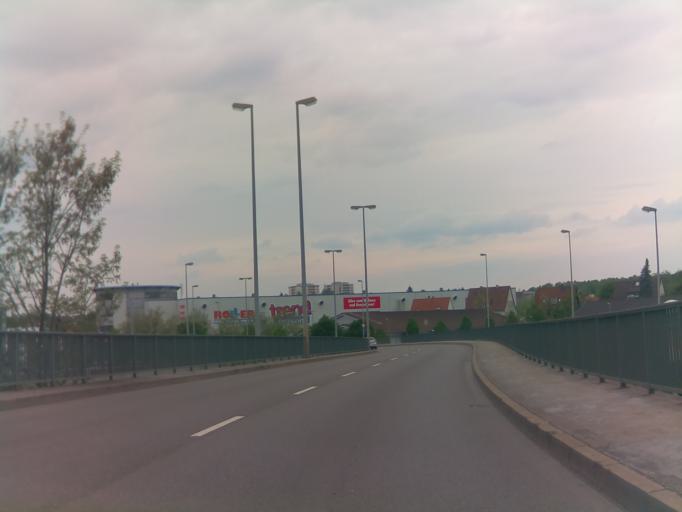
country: DE
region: Baden-Wuerttemberg
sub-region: Tuebingen Region
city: Reutlingen
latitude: 48.5013
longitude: 9.2110
